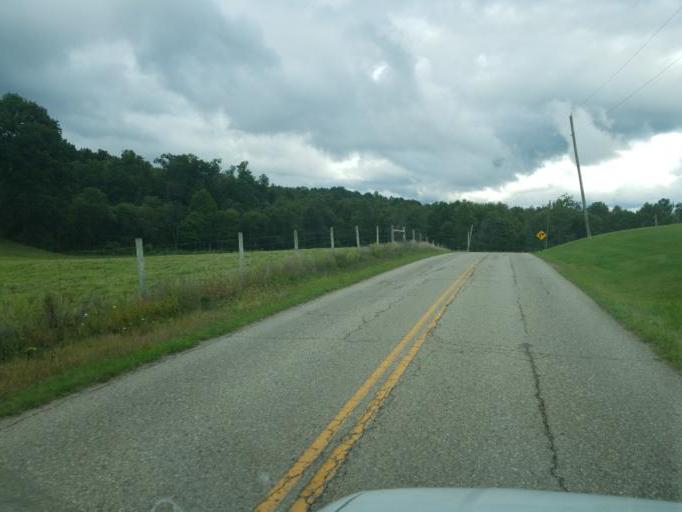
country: US
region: Ohio
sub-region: Jackson County
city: Oak Hill
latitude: 38.9388
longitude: -82.5796
